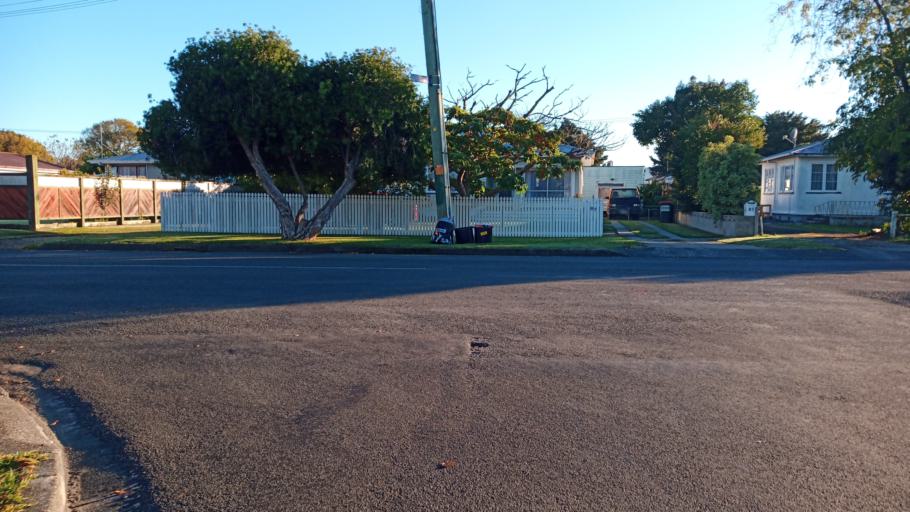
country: NZ
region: Gisborne
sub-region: Gisborne District
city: Gisborne
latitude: -38.6592
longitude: 177.9899
